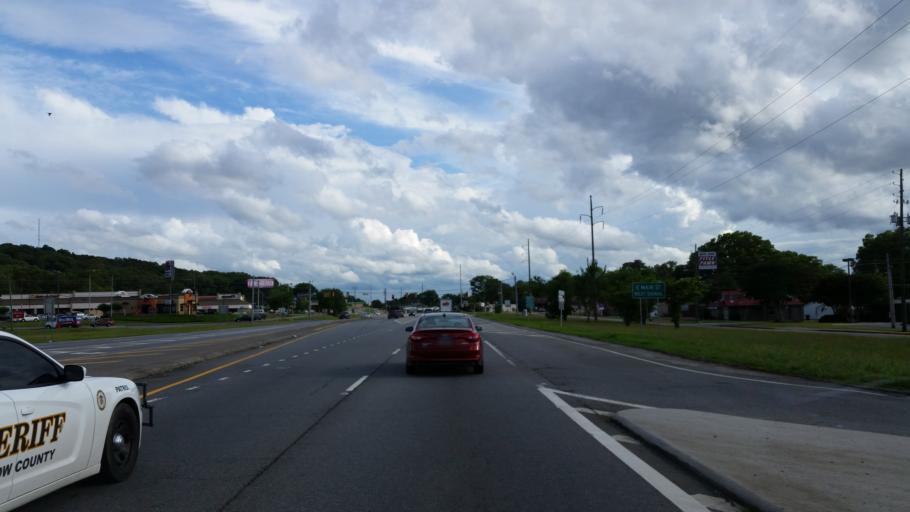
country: US
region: Georgia
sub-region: Bartow County
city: Cartersville
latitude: 34.1689
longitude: -84.7882
